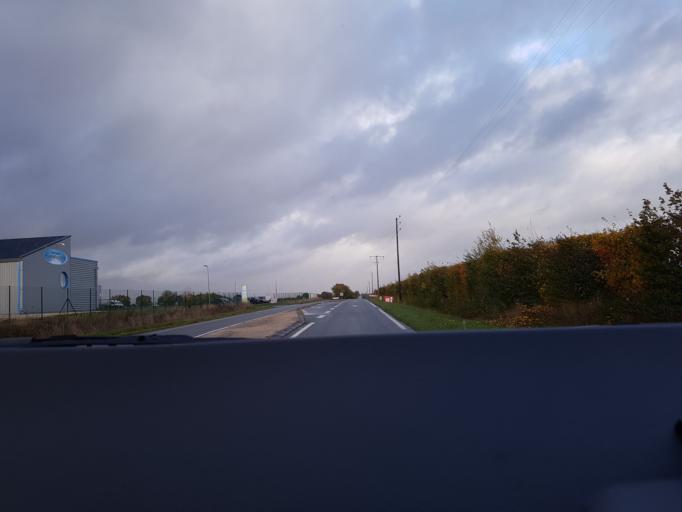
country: FR
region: Poitou-Charentes
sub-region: Departement des Deux-Sevres
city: Brioux-sur-Boutonne
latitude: 46.1564
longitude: -0.2080
